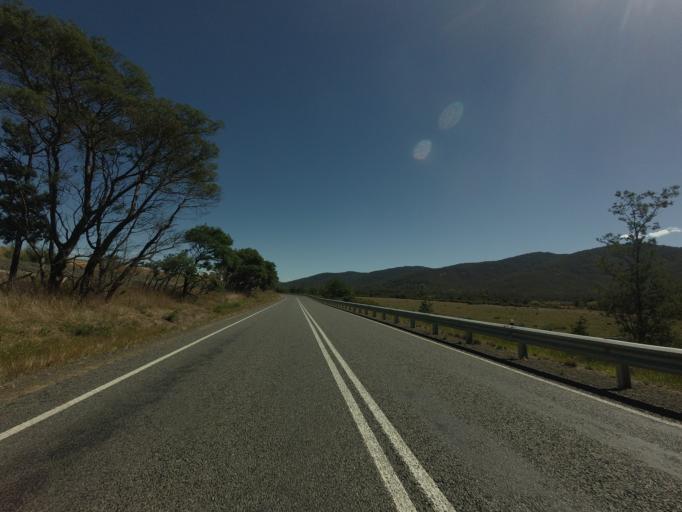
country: AU
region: Tasmania
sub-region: Northern Midlands
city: Evandale
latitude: -41.7391
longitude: 147.7972
